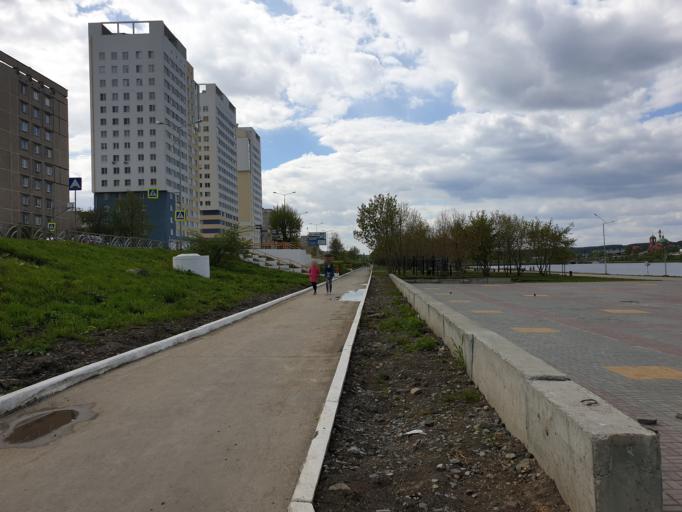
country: RU
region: Sverdlovsk
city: Pervoural'sk
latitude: 56.9142
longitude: 59.9447
